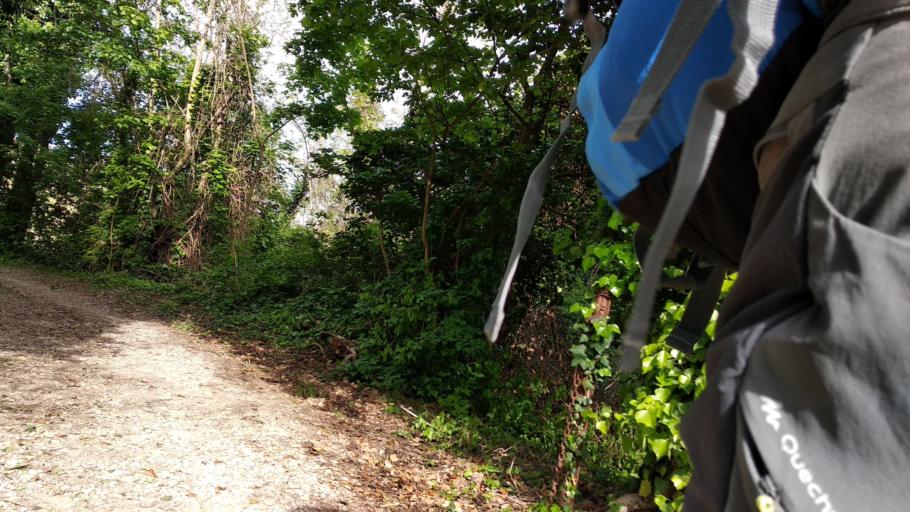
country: IT
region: Emilia-Romagna
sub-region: Provincia di Ravenna
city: Brisighella
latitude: 44.2252
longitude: 11.7557
